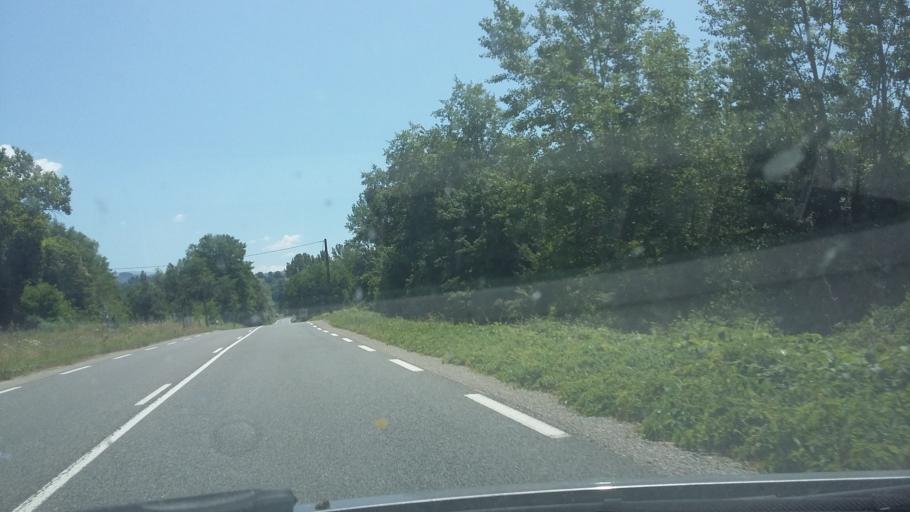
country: FR
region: Rhone-Alpes
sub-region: Departement de l'Ain
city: Belley
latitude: 45.7847
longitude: 5.6865
